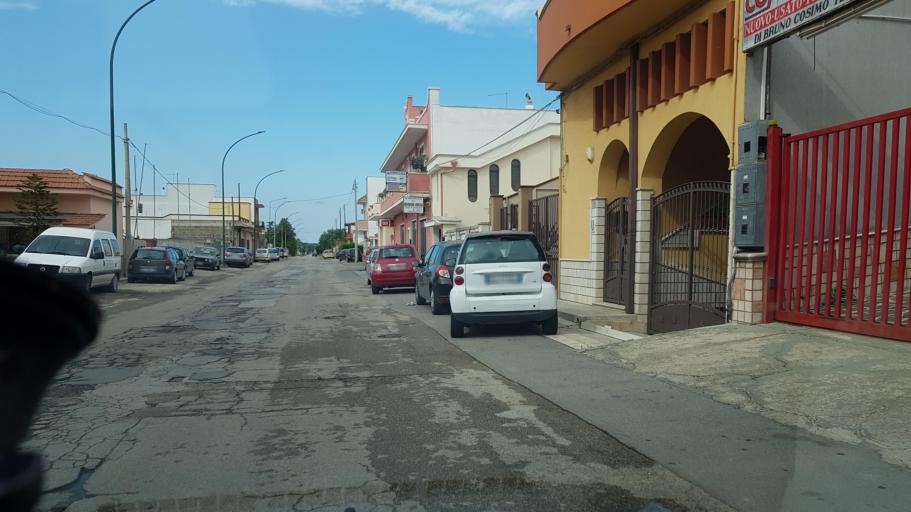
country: IT
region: Apulia
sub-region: Provincia di Brindisi
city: Torre Santa Susanna
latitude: 40.4736
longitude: 17.7399
